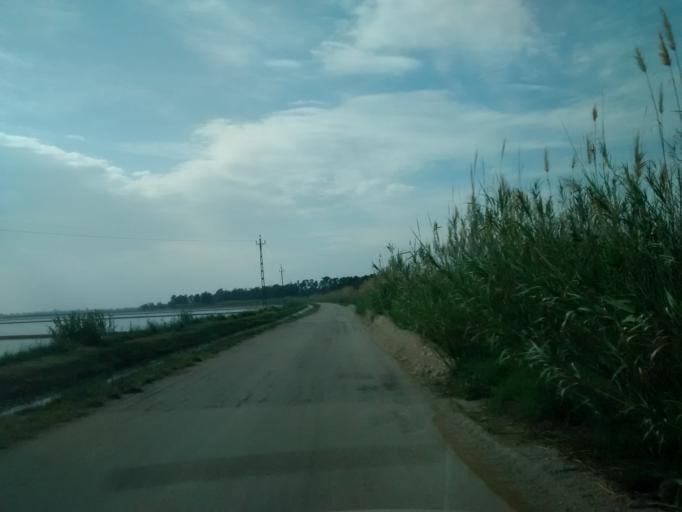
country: ES
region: Catalonia
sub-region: Provincia de Tarragona
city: Deltebre
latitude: 40.6949
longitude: 0.8382
